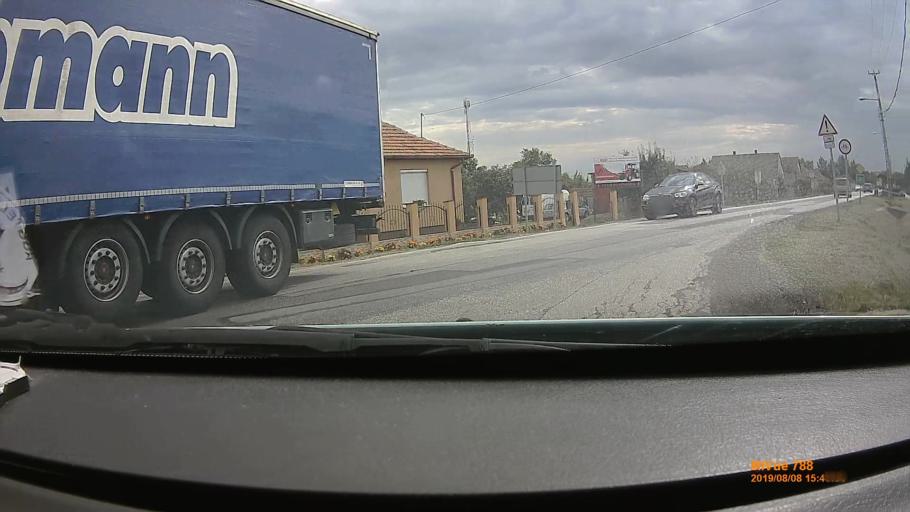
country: HU
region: Szabolcs-Szatmar-Bereg
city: Kocsord
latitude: 47.9383
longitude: 22.4288
